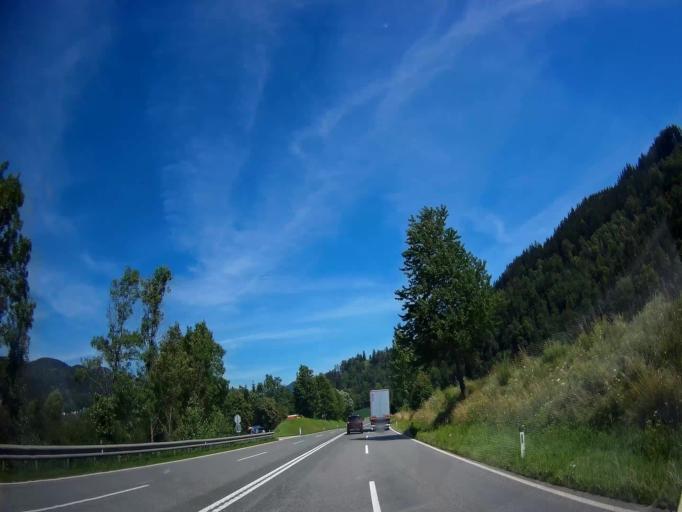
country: AT
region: Carinthia
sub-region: Politischer Bezirk Sankt Veit an der Glan
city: Micheldorf
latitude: 46.9098
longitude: 14.4370
